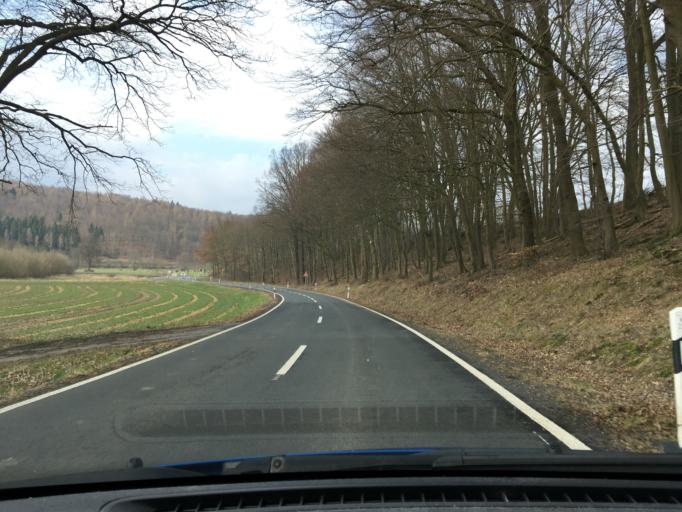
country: DE
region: Lower Saxony
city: Adelebsen
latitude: 51.5683
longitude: 9.7197
